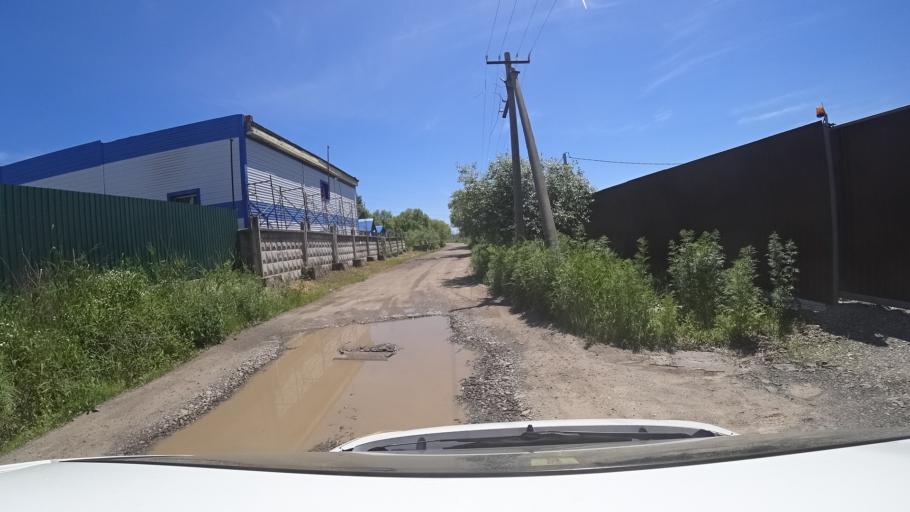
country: RU
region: Khabarovsk Krai
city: Topolevo
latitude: 48.5002
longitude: 135.1824
